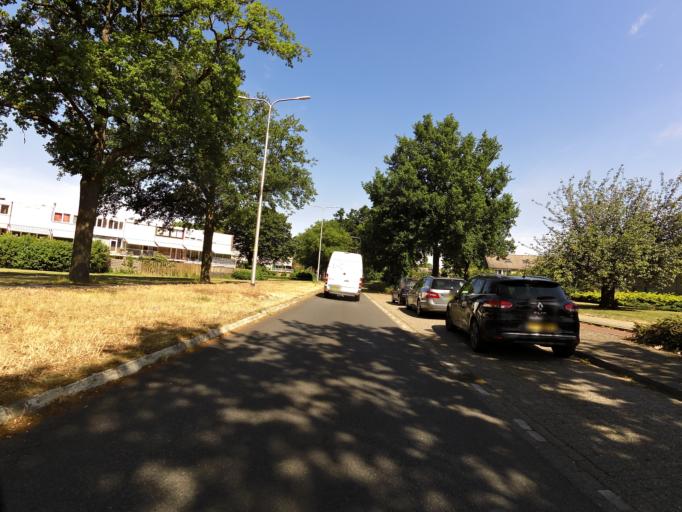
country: NL
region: Gelderland
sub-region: Gemeente Zevenaar
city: Zevenaar
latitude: 51.9344
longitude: 6.0662
